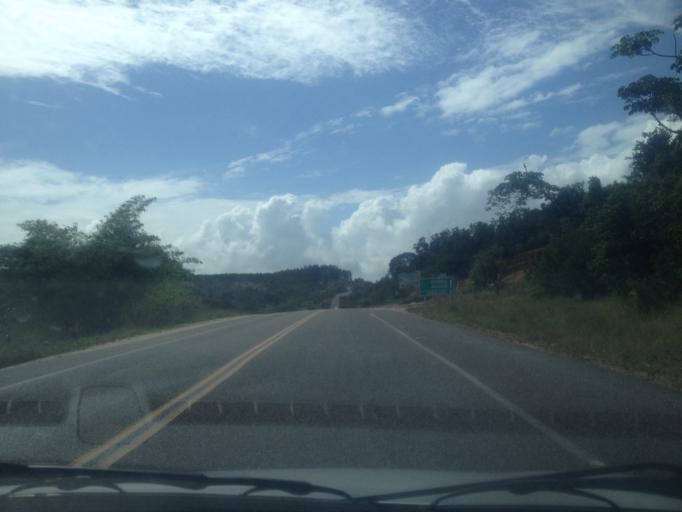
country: BR
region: Bahia
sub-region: Conde
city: Conde
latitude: -11.6714
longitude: -37.5608
